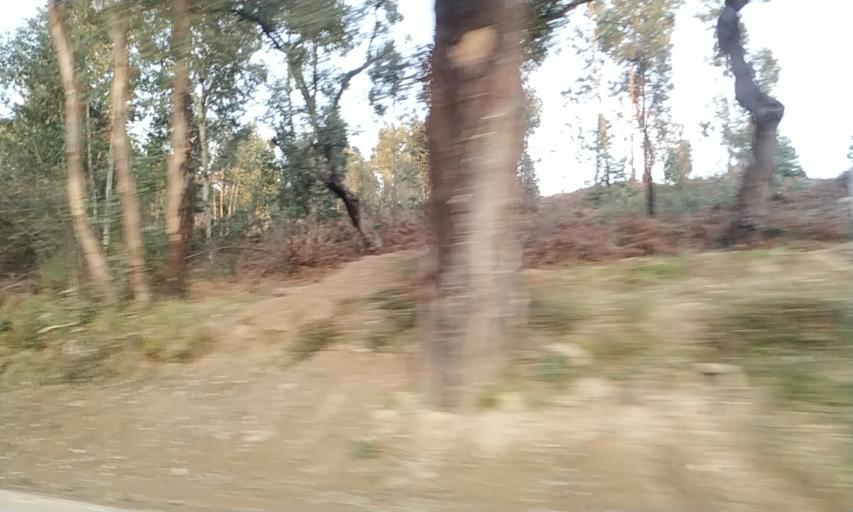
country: PT
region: Vila Real
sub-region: Mondim de Basto
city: Mondim de Basto
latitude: 41.4500
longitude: -7.9619
